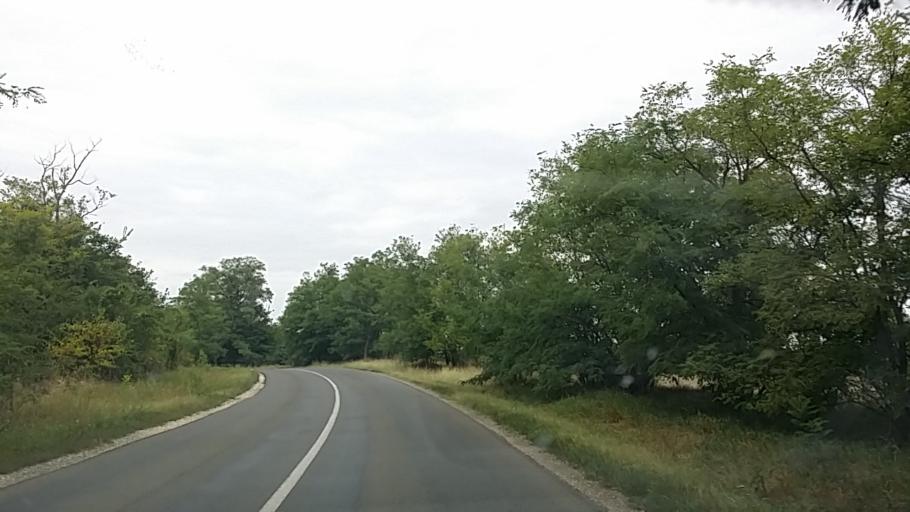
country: HU
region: Komarom-Esztergom
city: Naszaly
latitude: 47.6842
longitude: 18.2359
